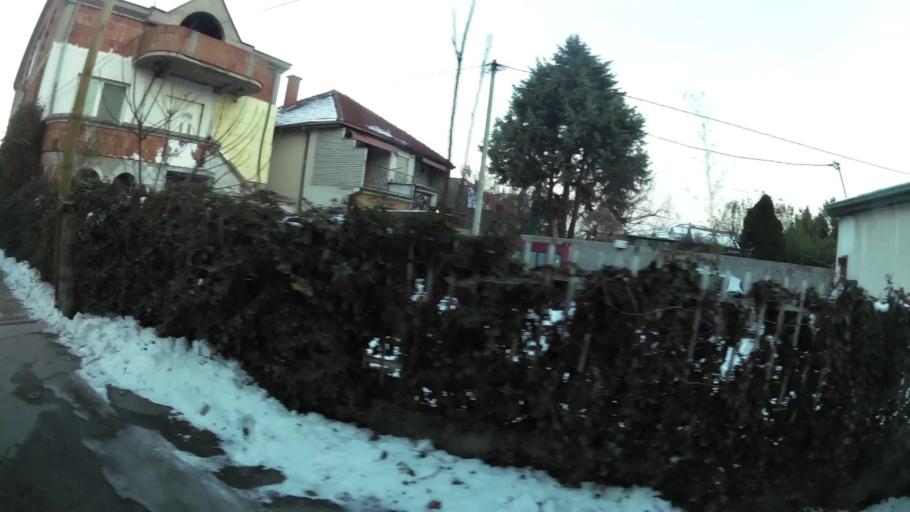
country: MK
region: Kisela Voda
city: Usje
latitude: 41.9814
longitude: 21.4858
